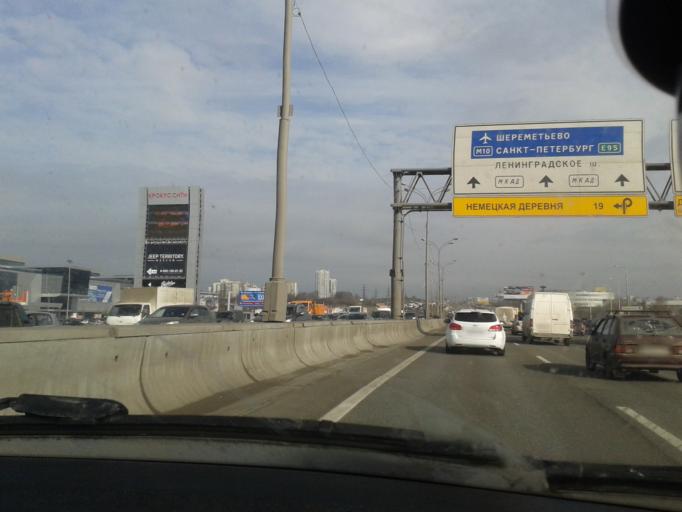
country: RU
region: Moscow
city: Strogino
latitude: 55.8236
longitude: 37.3931
